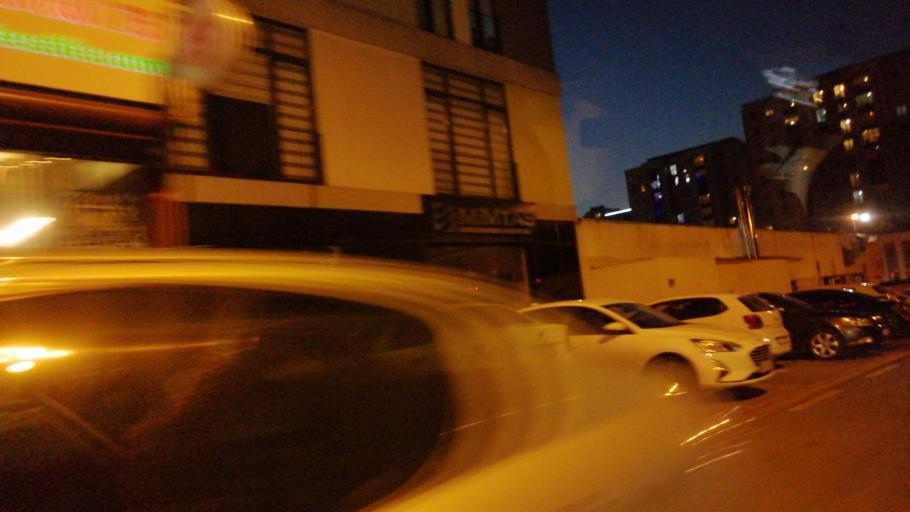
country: TR
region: Istanbul
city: Umraniye
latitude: 40.9995
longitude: 29.1409
